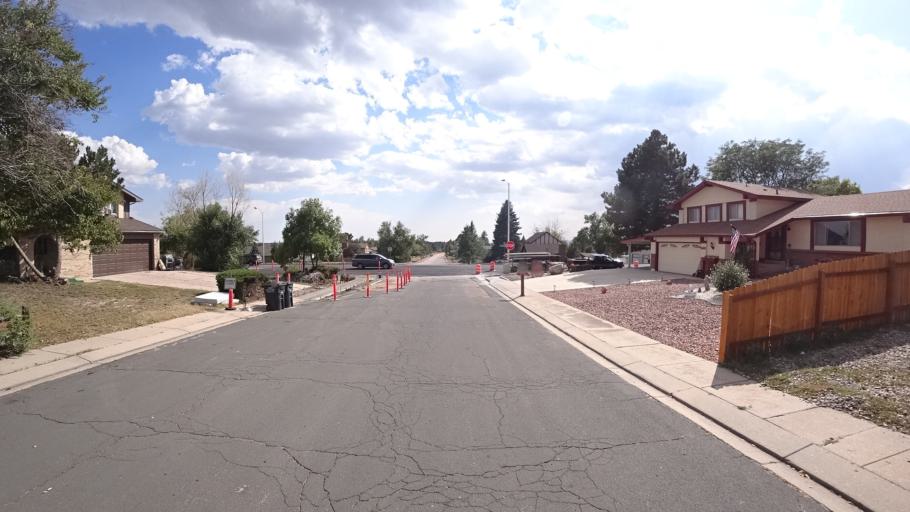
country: US
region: Colorado
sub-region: El Paso County
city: Cimarron Hills
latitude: 38.8683
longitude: -104.7295
